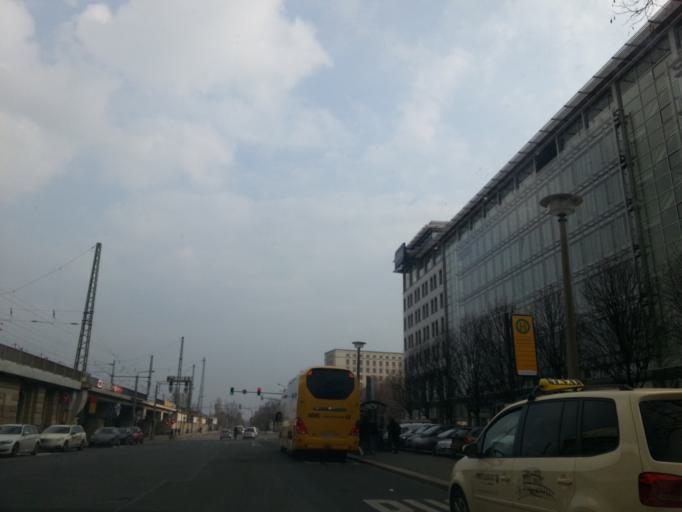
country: DE
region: Saxony
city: Dresden
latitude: 51.0394
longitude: 13.7318
